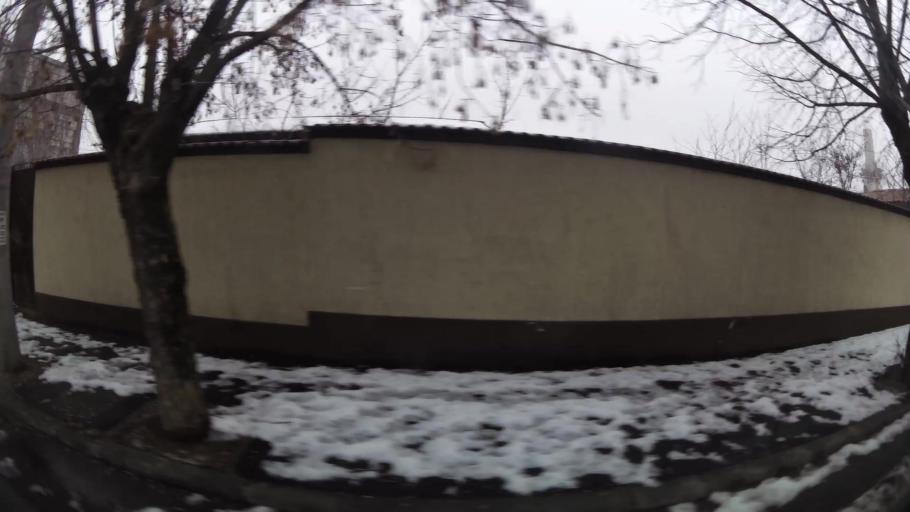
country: RO
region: Ilfov
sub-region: Comuna Chiajna
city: Rosu
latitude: 44.4699
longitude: 26.0329
